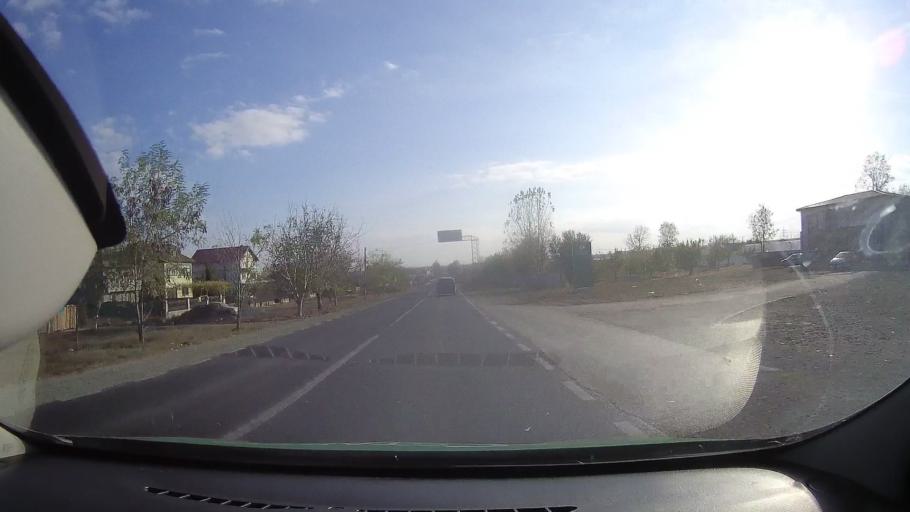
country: RO
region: Constanta
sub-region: Comuna Lumina
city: Lumina
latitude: 44.2869
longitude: 28.5566
